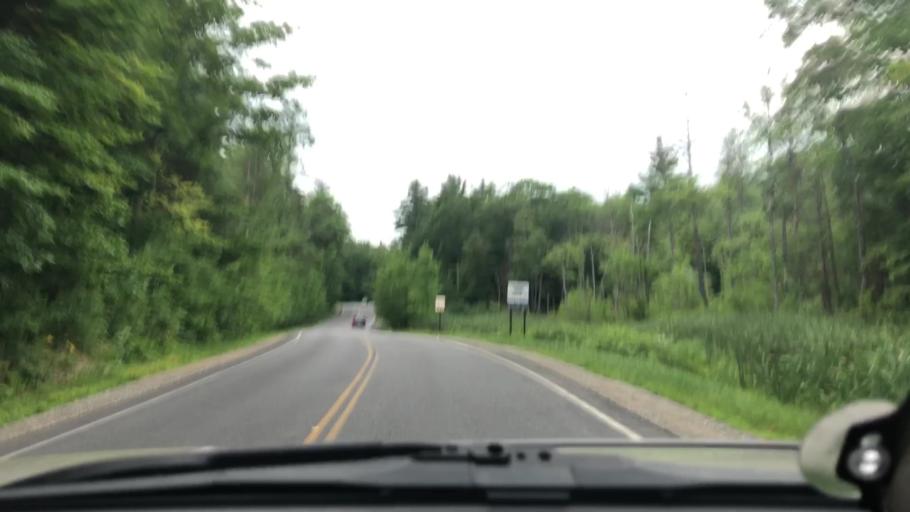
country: US
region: New York
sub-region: Saratoga County
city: Corinth
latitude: 43.1992
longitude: -73.7622
